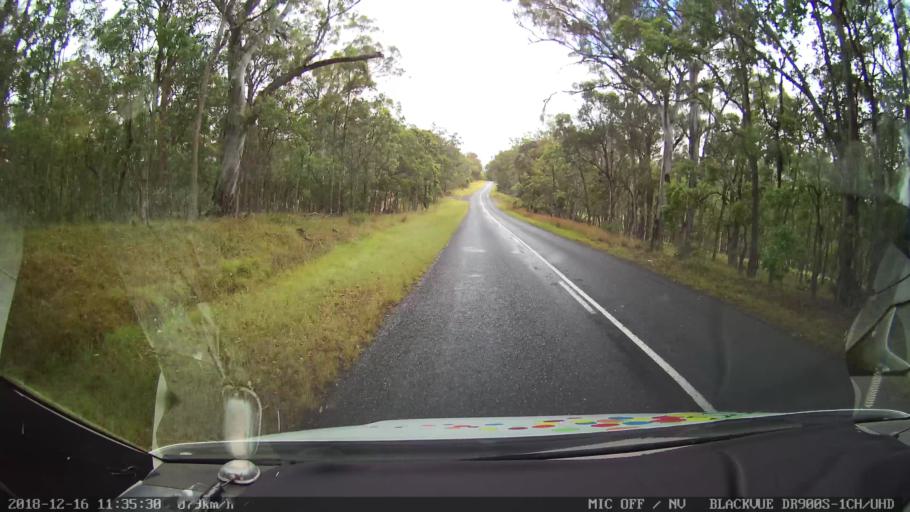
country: AU
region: New South Wales
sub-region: Tenterfield Municipality
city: Carrolls Creek
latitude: -28.9894
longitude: 152.1629
